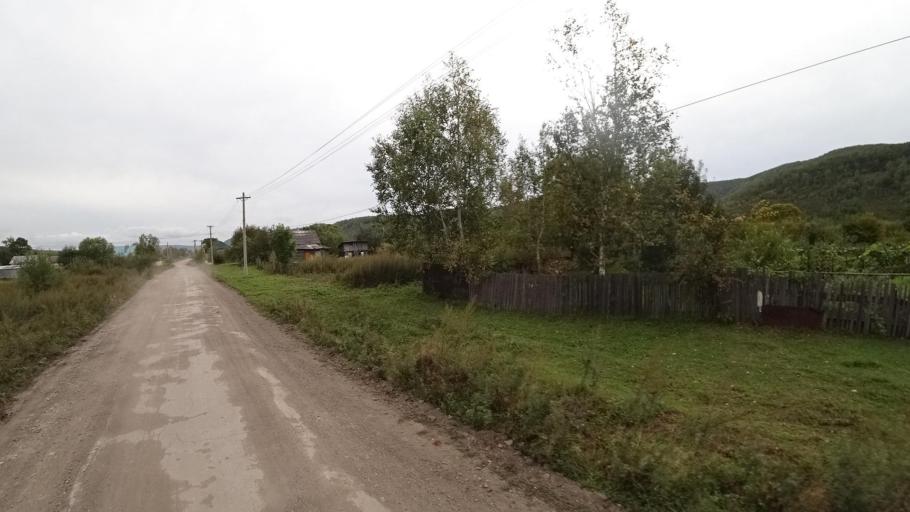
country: RU
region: Jewish Autonomous Oblast
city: Khingansk
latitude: 49.0374
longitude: 131.0496
